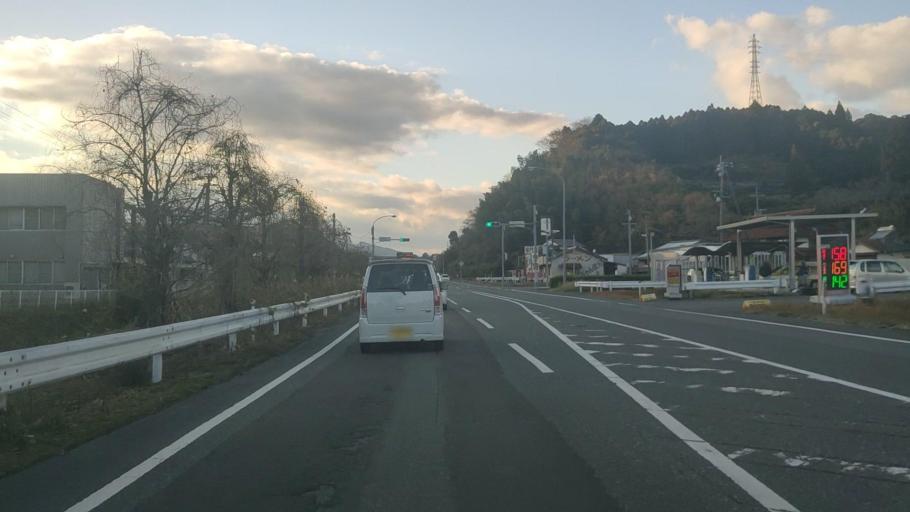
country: JP
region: Saga Prefecture
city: Takeocho-takeo
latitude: 33.2893
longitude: 130.1308
